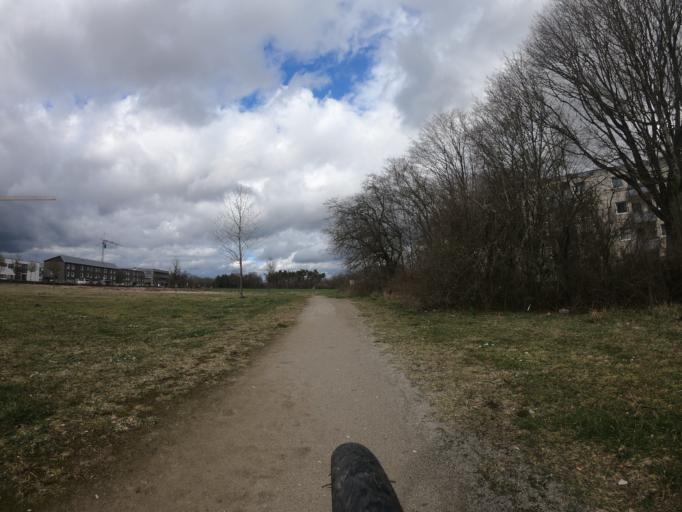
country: DE
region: Bavaria
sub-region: Upper Bavaria
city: Fuerstenfeldbruck
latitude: 48.1697
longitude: 11.2279
